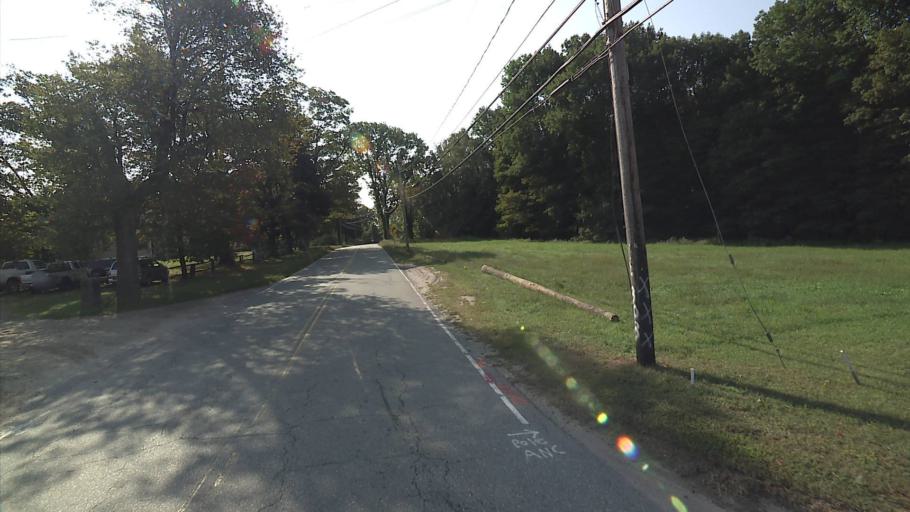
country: US
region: Connecticut
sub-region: Windham County
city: South Windham
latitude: 41.6271
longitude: -72.1989
